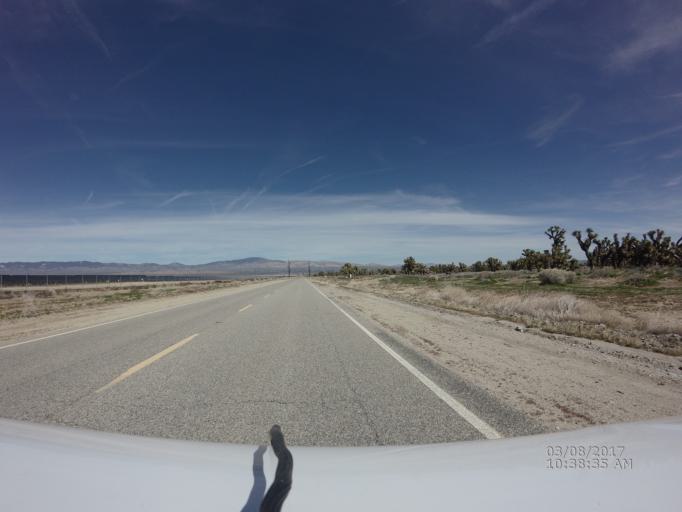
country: US
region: California
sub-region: Los Angeles County
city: Green Valley
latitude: 34.7919
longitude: -118.4314
